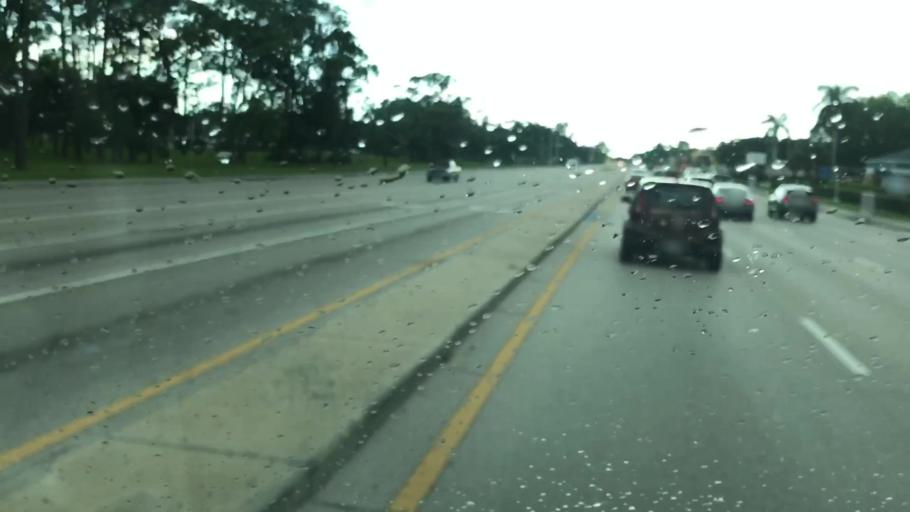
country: US
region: Florida
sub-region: Lee County
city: Whiskey Creek
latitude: 26.5572
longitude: -81.8867
